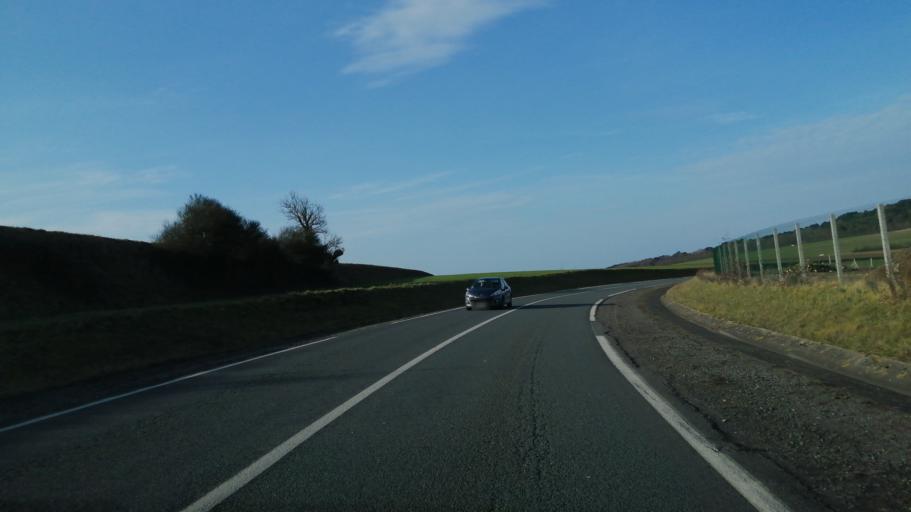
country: FR
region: Nord-Pas-de-Calais
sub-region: Departement du Pas-de-Calais
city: Neufchatel-Hardelot
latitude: 50.6090
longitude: 1.6423
